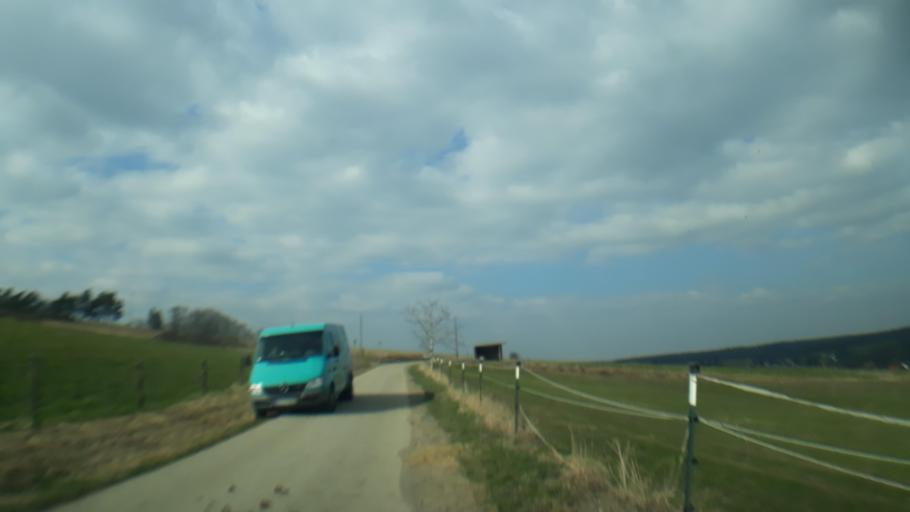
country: DE
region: Rheinland-Pfalz
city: Kirchsahr
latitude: 50.5845
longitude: 6.8970
